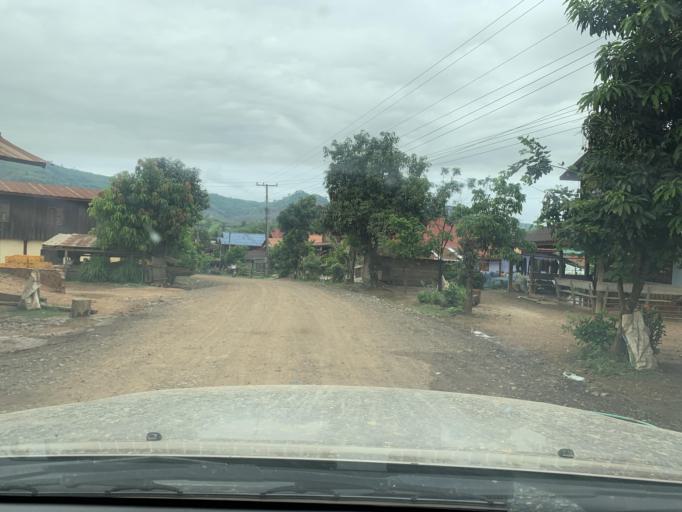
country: TH
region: Nan
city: Mae Charim
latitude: 18.4207
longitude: 101.4501
